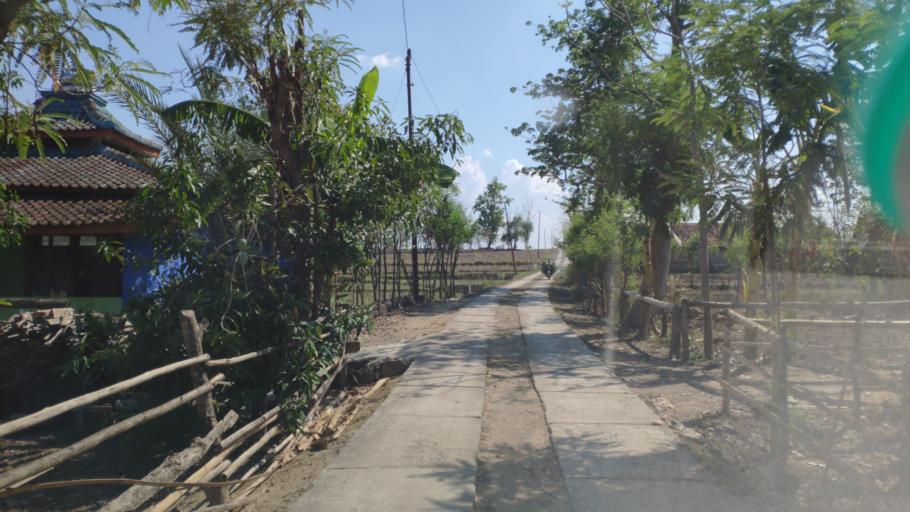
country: ID
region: Central Java
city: Botoh
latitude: -7.0865
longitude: 111.4655
